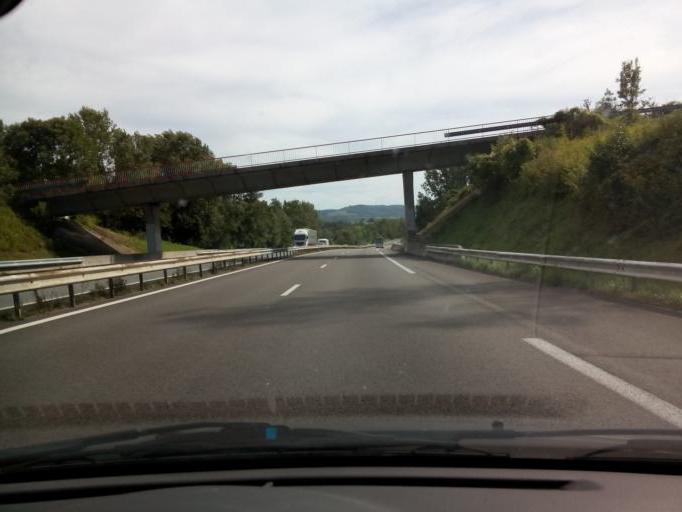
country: FR
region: Rhone-Alpes
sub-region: Departement de l'Isere
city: Saint-Victor-de-Cessieu
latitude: 45.5259
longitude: 5.4103
